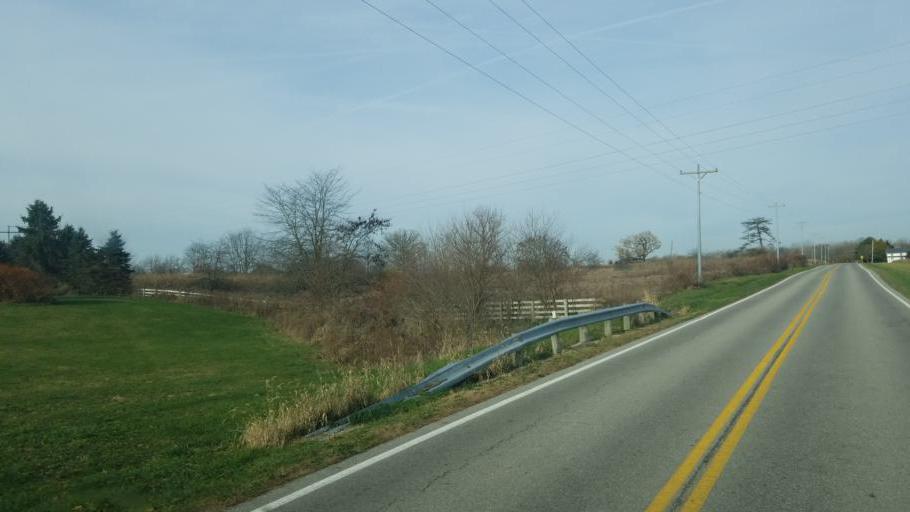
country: US
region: Ohio
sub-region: Madison County
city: Plain City
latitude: 40.1426
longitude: -83.3482
